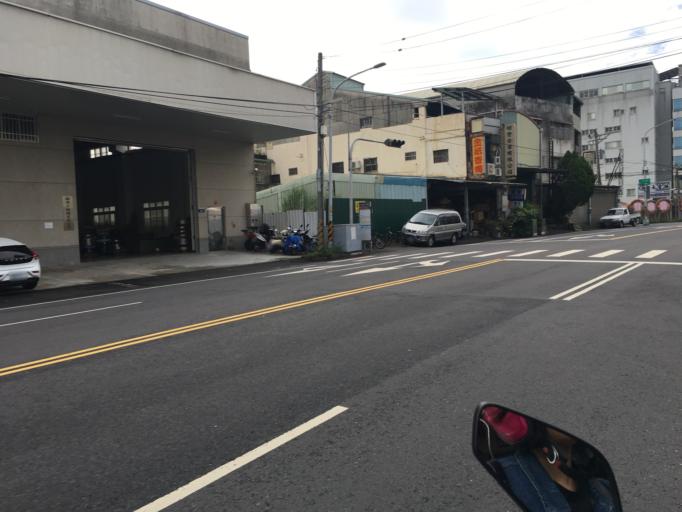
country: TW
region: Taiwan
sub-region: Taichung City
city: Taichung
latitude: 24.0967
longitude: 120.6869
